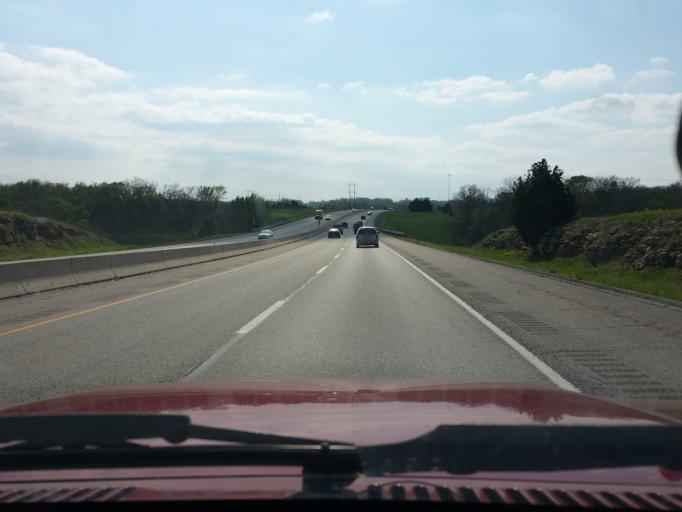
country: US
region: Kansas
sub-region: Douglas County
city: Lawrence
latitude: 38.9975
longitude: -95.3266
